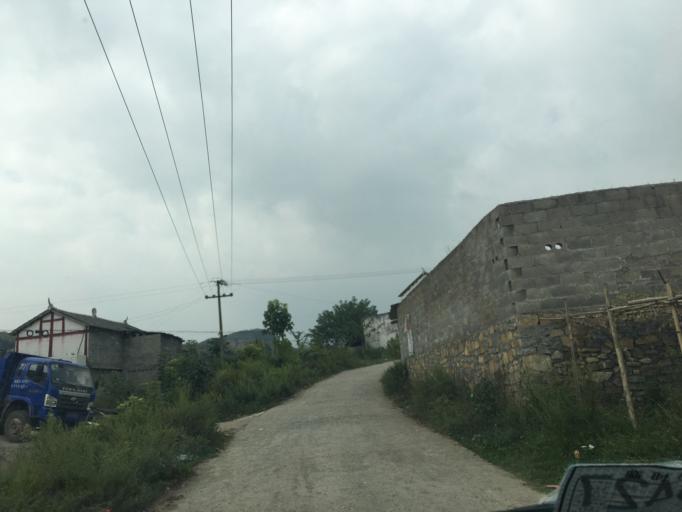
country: CN
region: Guangxi Zhuangzu Zizhiqu
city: Xinzhou
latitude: 25.5708
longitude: 105.6181
